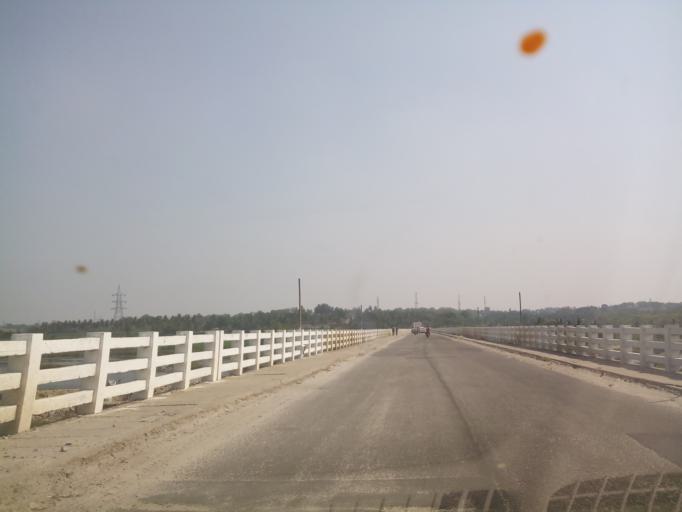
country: IN
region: Karnataka
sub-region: Mandya
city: Shrirangapattana
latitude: 12.4262
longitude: 76.5816
